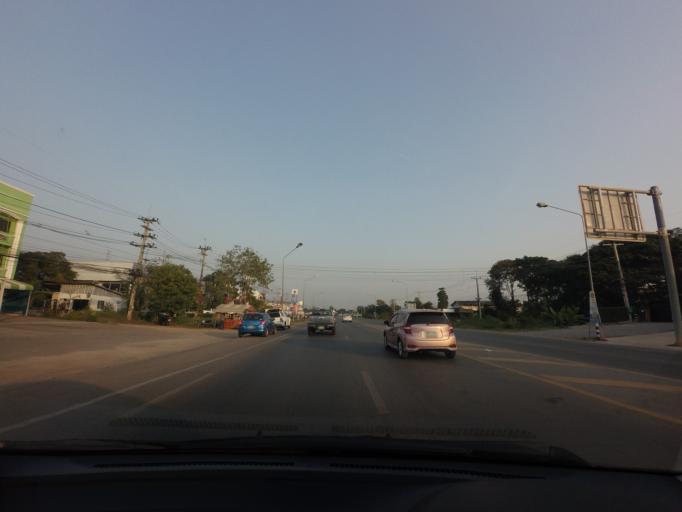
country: TH
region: Sukhothai
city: Sukhothai
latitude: 17.0210
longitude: 99.8227
